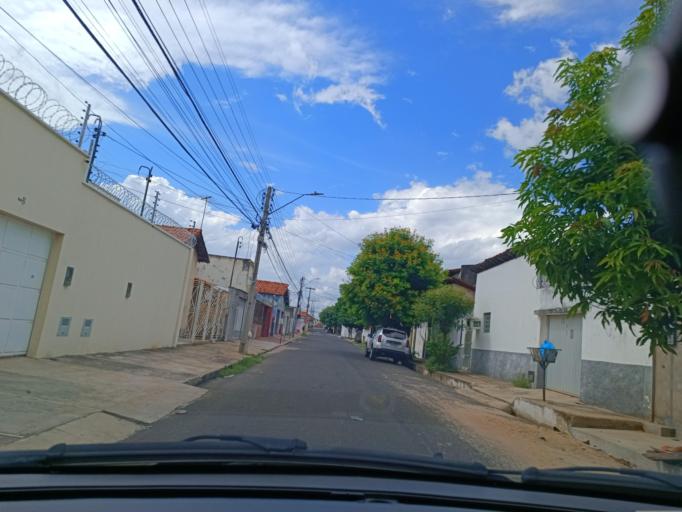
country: BR
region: Piaui
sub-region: Teresina
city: Teresina
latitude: -5.0828
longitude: -42.8154
